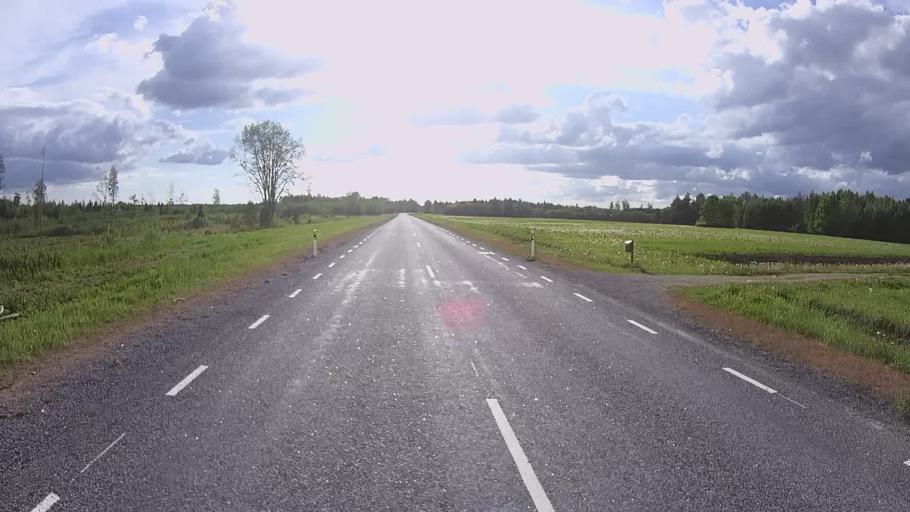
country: EE
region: Jogevamaa
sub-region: Mustvee linn
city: Mustvee
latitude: 59.0259
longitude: 27.0047
